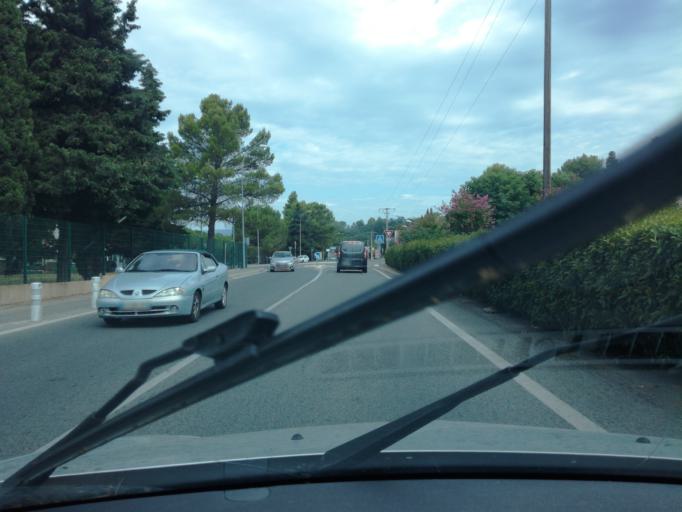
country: FR
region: Provence-Alpes-Cote d'Azur
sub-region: Departement du Var
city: Draguignan
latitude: 43.5244
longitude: 6.4611
